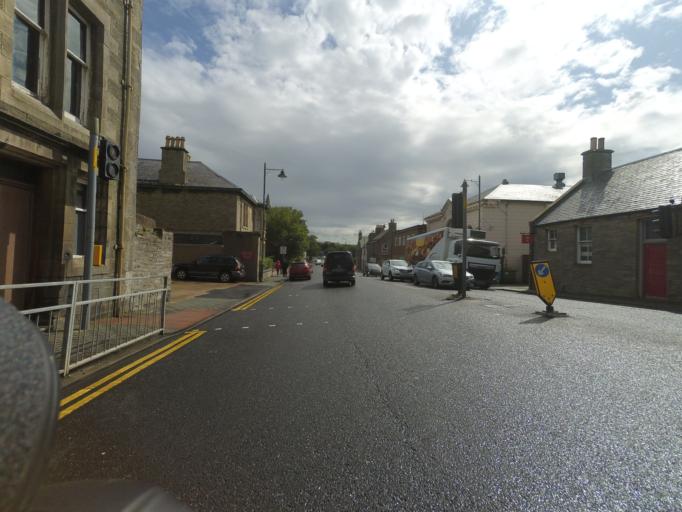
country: GB
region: Scotland
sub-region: Highland
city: Thurso
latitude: 58.5934
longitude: -3.5218
